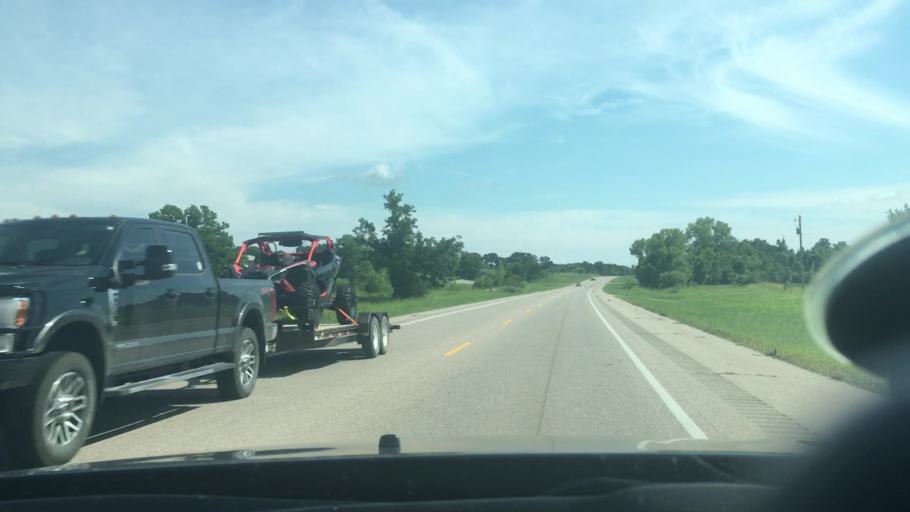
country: US
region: Oklahoma
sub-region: Seminole County
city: Seminole
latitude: 35.1775
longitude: -96.6743
